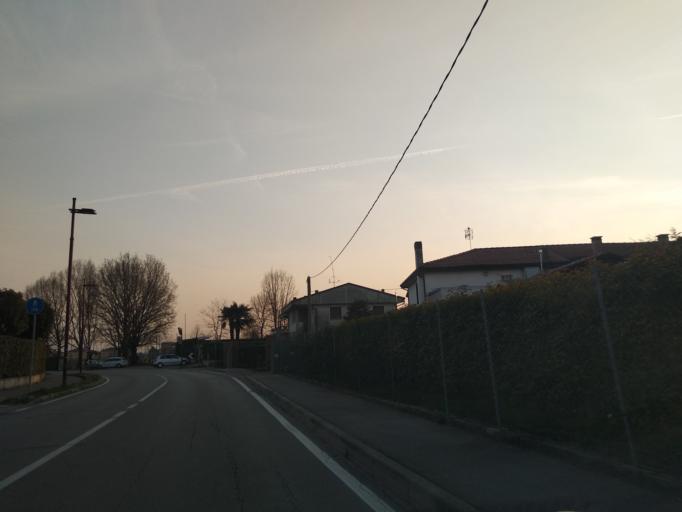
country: IT
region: Veneto
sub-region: Provincia di Padova
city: Sarmeola
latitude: 45.4303
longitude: 11.8087
